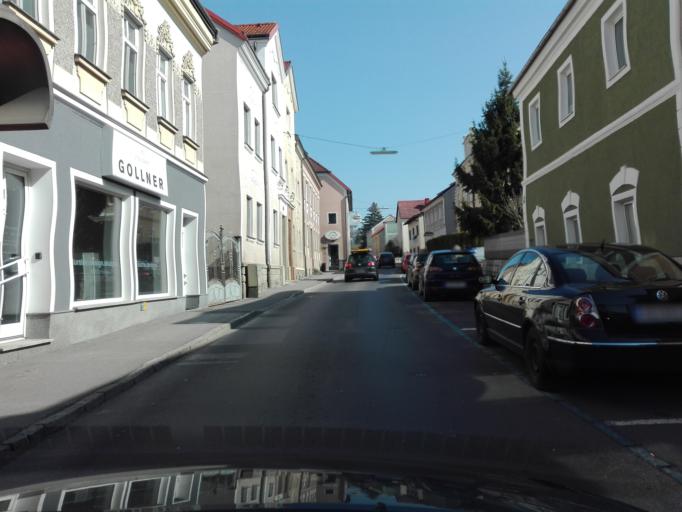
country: AT
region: Upper Austria
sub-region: Politischer Bezirk Urfahr-Umgebung
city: Gallneukirchen
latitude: 48.3543
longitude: 14.4172
